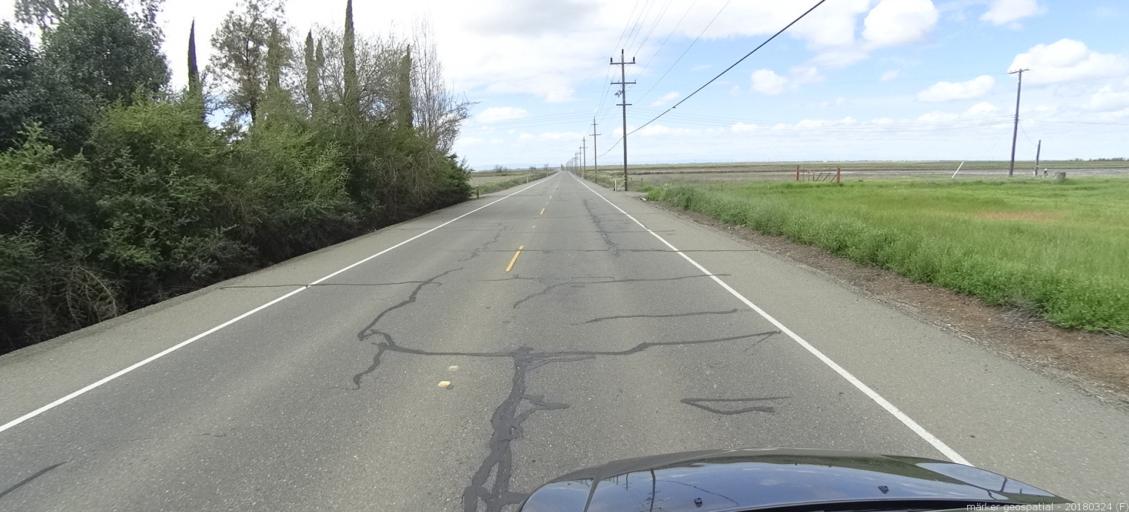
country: US
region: California
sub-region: Sacramento County
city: Elverta
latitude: 38.7145
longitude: -121.4930
